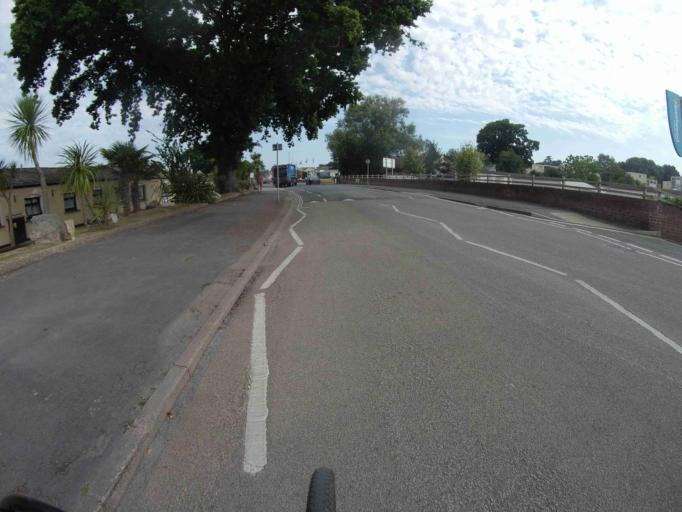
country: GB
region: England
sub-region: Devon
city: Dawlish
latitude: 50.6000
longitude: -3.4477
